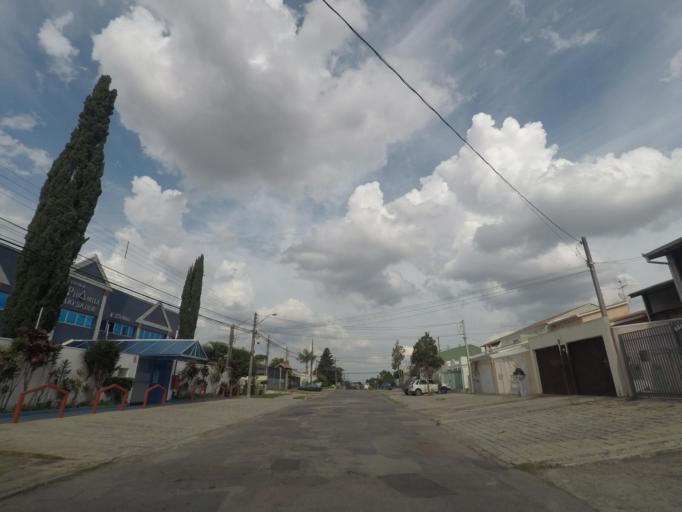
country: BR
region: Parana
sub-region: Curitiba
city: Curitiba
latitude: -25.4866
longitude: -49.2587
